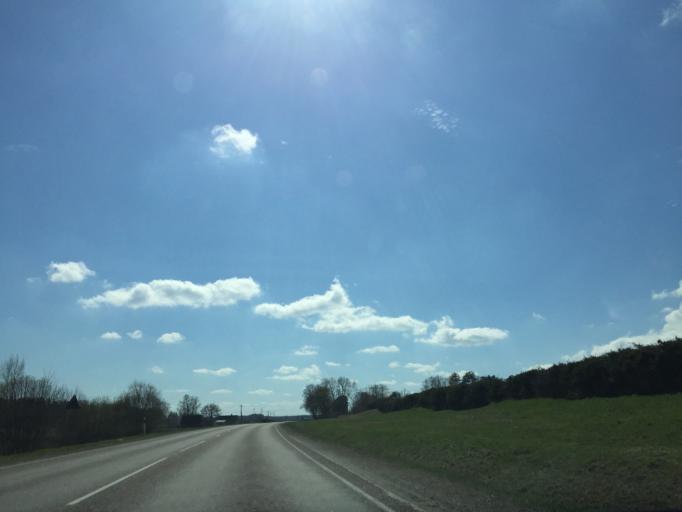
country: EE
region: Valgamaa
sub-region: Torva linn
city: Torva
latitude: 58.0386
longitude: 26.1846
